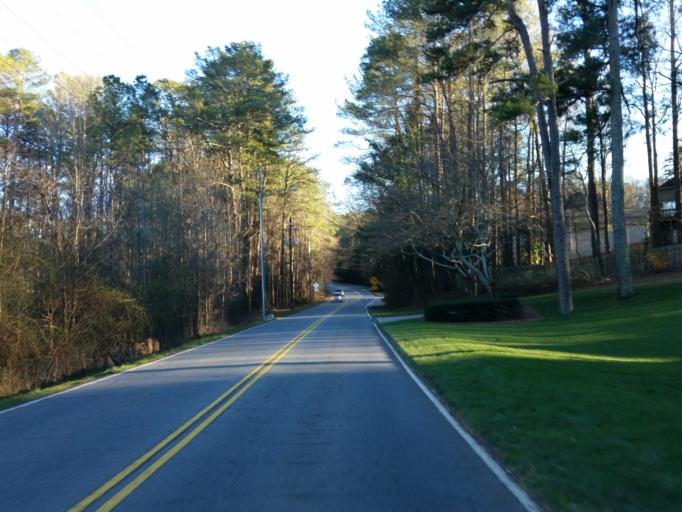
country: US
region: Georgia
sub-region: Cobb County
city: Marietta
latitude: 33.9588
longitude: -84.5840
